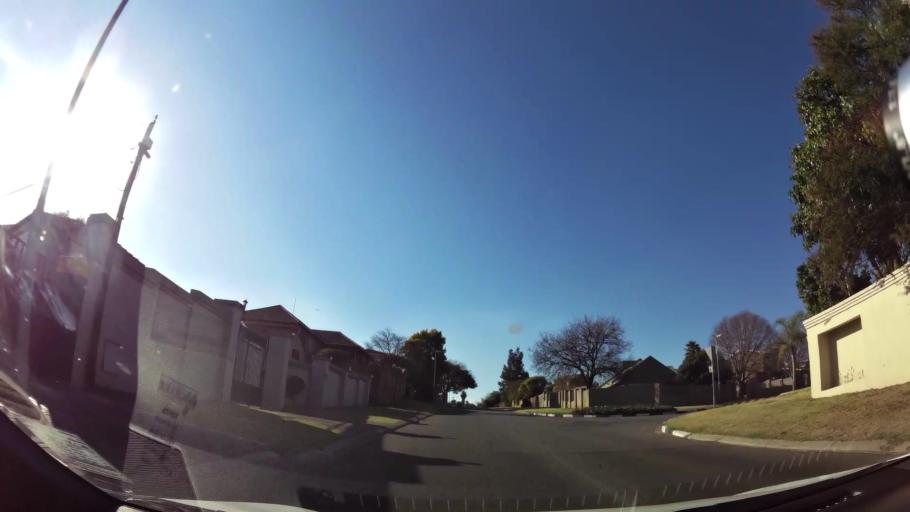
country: ZA
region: Gauteng
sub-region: City of Johannesburg Metropolitan Municipality
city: Johannesburg
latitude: -26.2958
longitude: 28.0605
